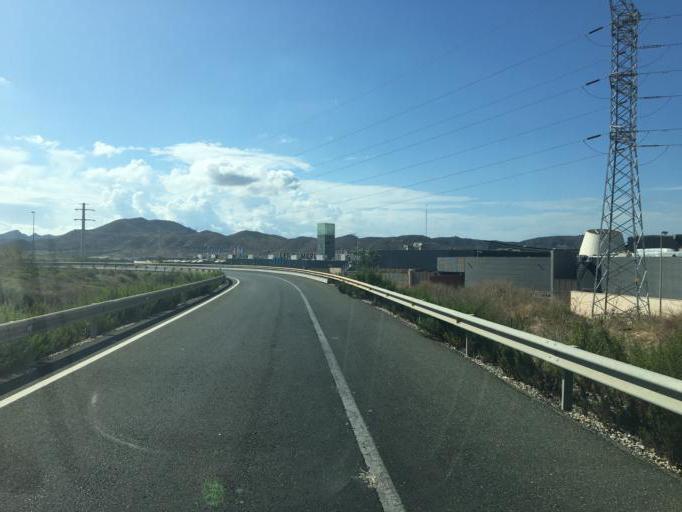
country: ES
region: Murcia
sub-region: Murcia
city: Cartagena
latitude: 37.6278
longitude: -0.9485
